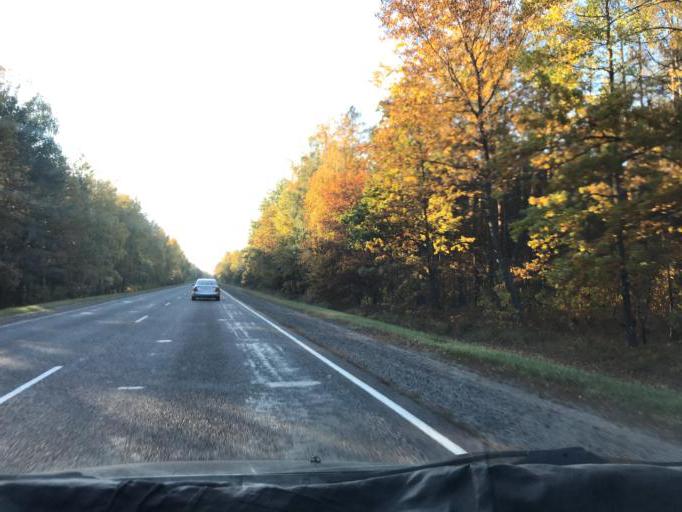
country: BY
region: Gomel
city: Zhytkavichy
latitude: 52.2729
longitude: 28.0866
